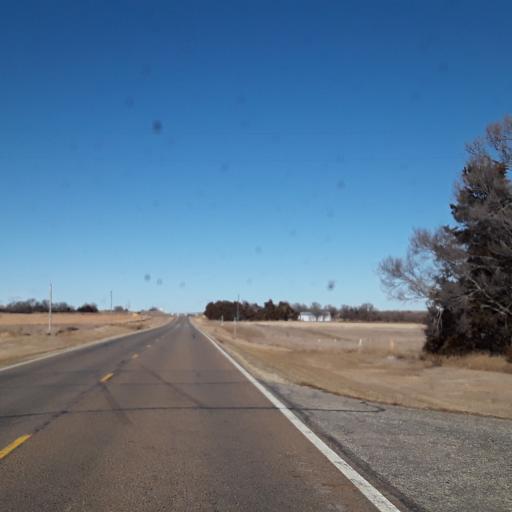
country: US
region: Kansas
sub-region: Lincoln County
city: Lincoln
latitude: 38.9845
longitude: -98.1512
